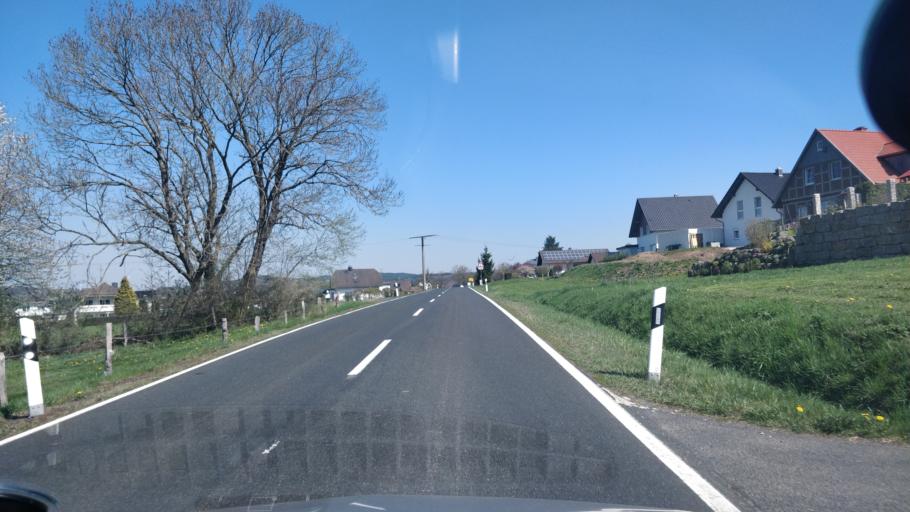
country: DE
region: Rheinland-Pfalz
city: Niederrossbach
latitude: 50.6264
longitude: 8.0380
